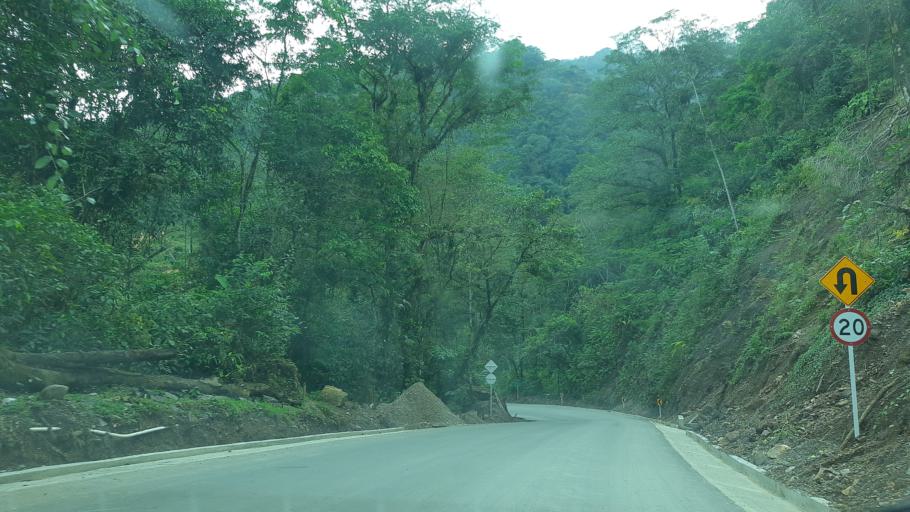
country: CO
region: Boyaca
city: Santa Maria
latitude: 4.8599
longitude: -73.2346
